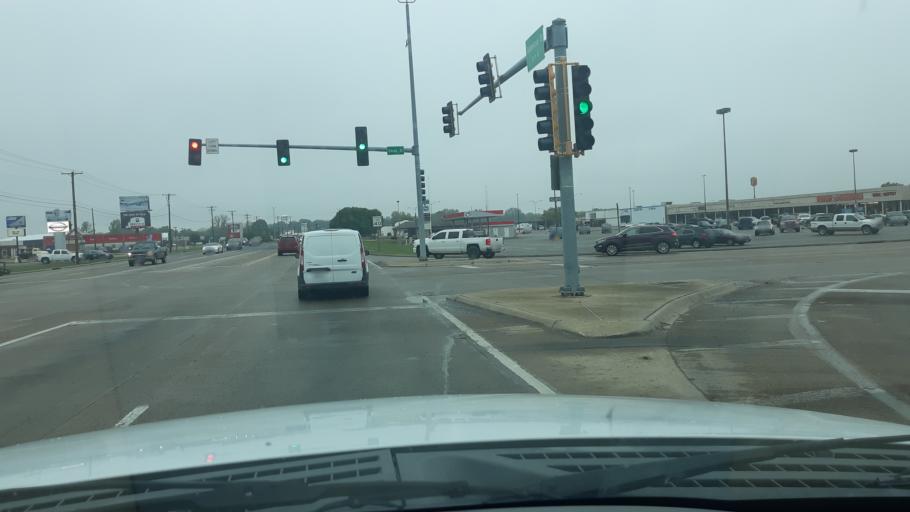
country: US
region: Illinois
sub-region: Saline County
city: Harrisburg
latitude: 37.7453
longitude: -88.5239
